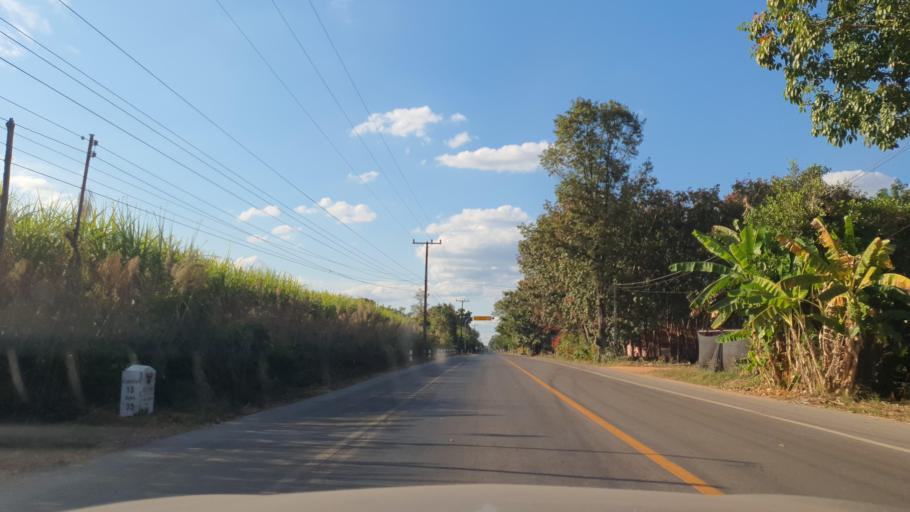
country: TH
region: Nong Khai
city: Bueng Khong Long
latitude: 18.0322
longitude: 103.9895
